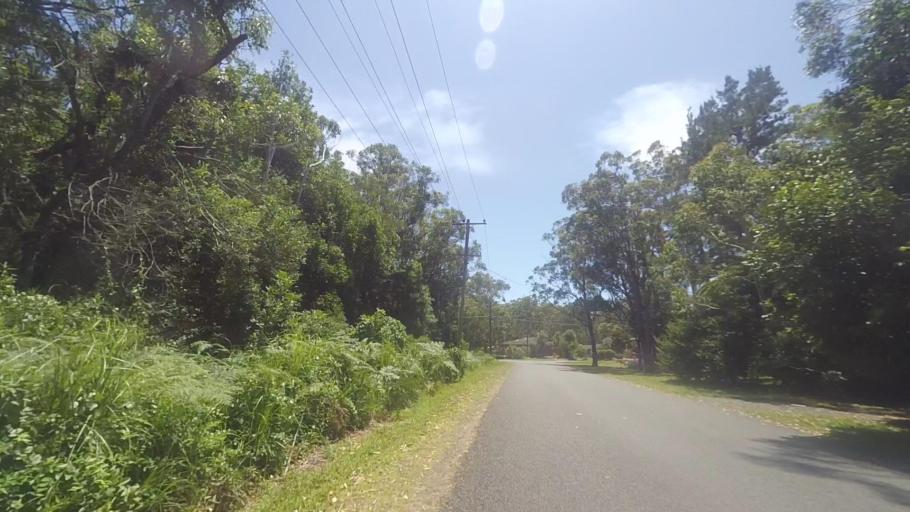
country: AU
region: New South Wales
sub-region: Great Lakes
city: Hawks Nest
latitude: -32.6658
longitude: 152.1752
